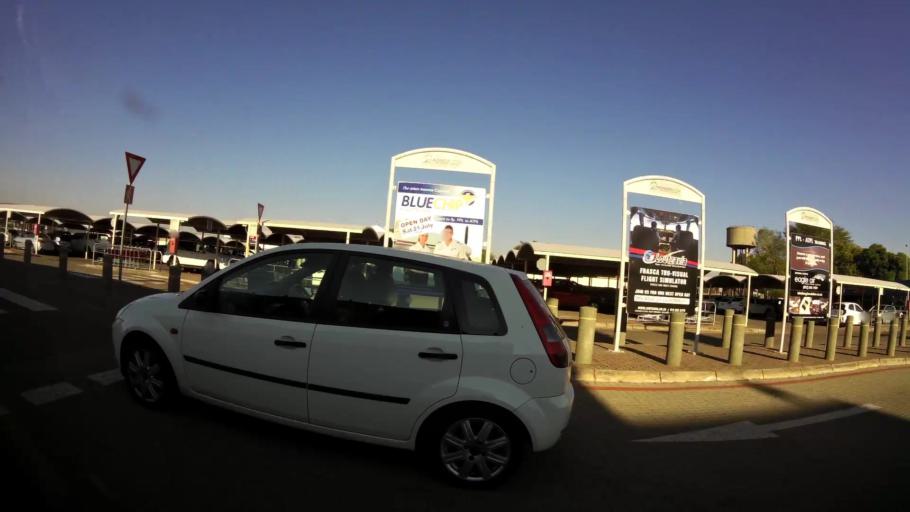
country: ZA
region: Gauteng
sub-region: City of Tshwane Metropolitan Municipality
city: Pretoria
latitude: -25.6575
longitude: 28.2144
